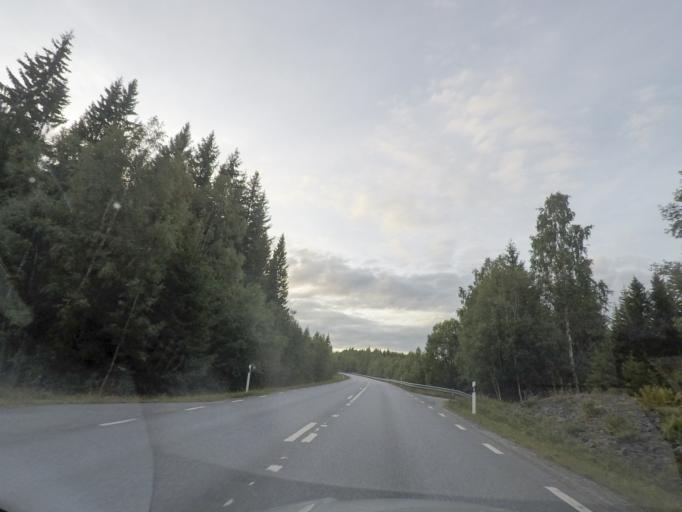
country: SE
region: OErebro
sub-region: Hallefors Kommun
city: Haellefors
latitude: 59.6590
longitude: 14.5739
